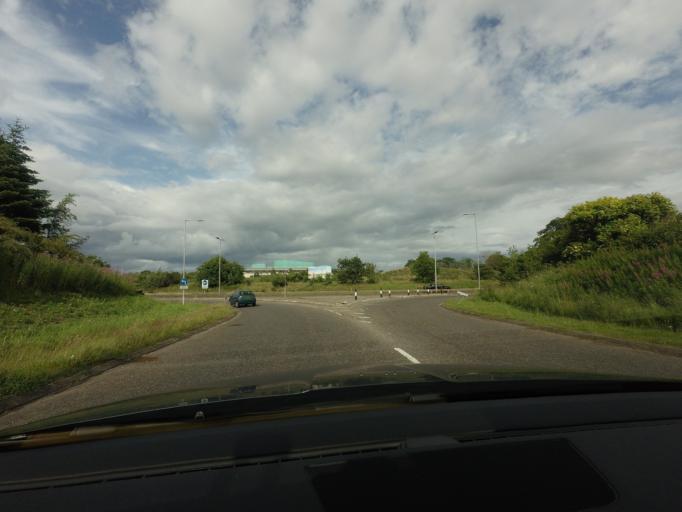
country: GB
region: Scotland
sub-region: Highland
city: Inverness
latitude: 57.4740
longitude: -4.1872
